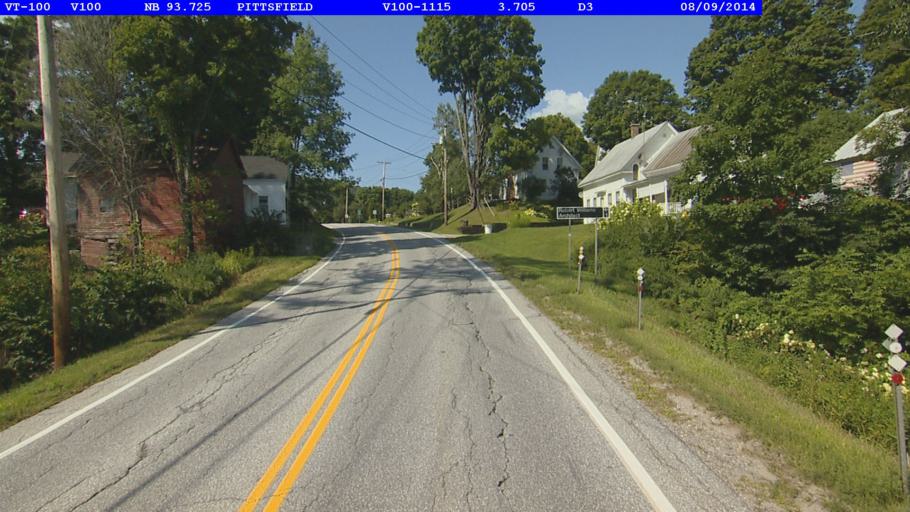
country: US
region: Vermont
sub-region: Orange County
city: Randolph
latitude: 43.7689
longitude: -72.8130
